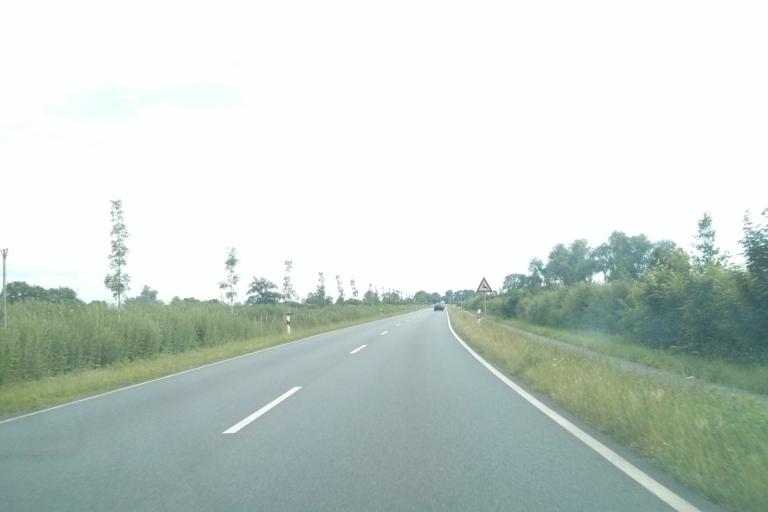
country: DE
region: Lower Saxony
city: Achim
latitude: 52.9916
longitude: 9.0531
